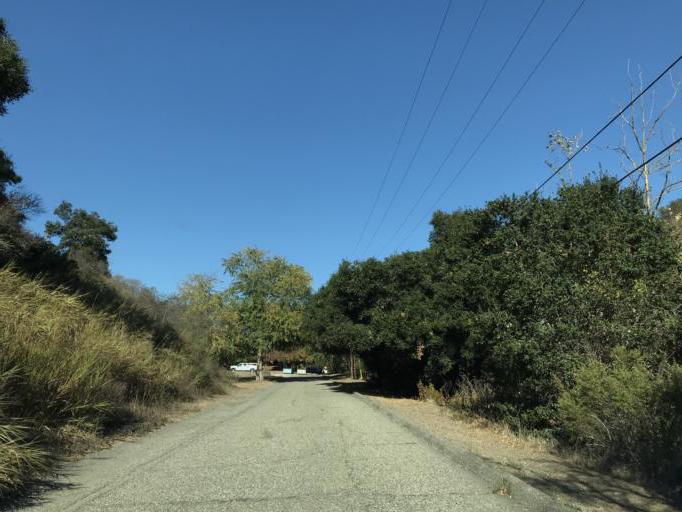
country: US
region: California
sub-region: Santa Barbara County
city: Goleta
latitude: 34.4483
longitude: -119.7779
